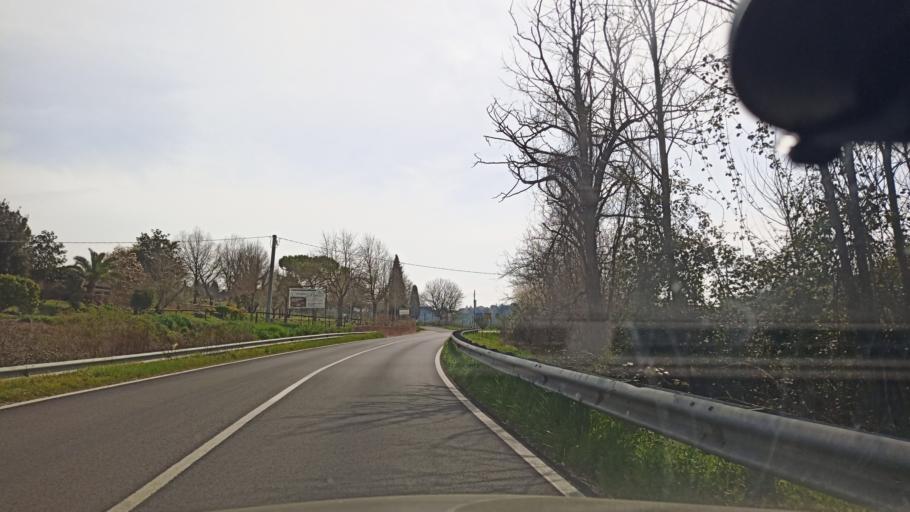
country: IT
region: Latium
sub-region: Provincia di Rieti
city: Cantalupo in Sabina
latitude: 42.3196
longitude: 12.6449
